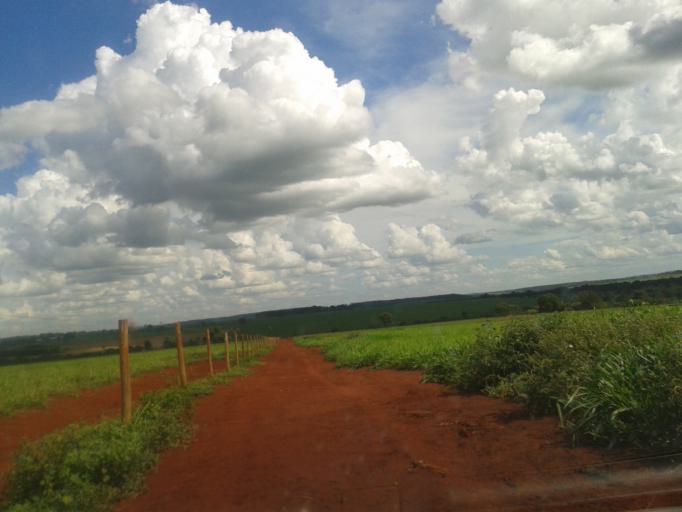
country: BR
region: Minas Gerais
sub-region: Capinopolis
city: Capinopolis
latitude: -18.7776
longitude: -49.8261
